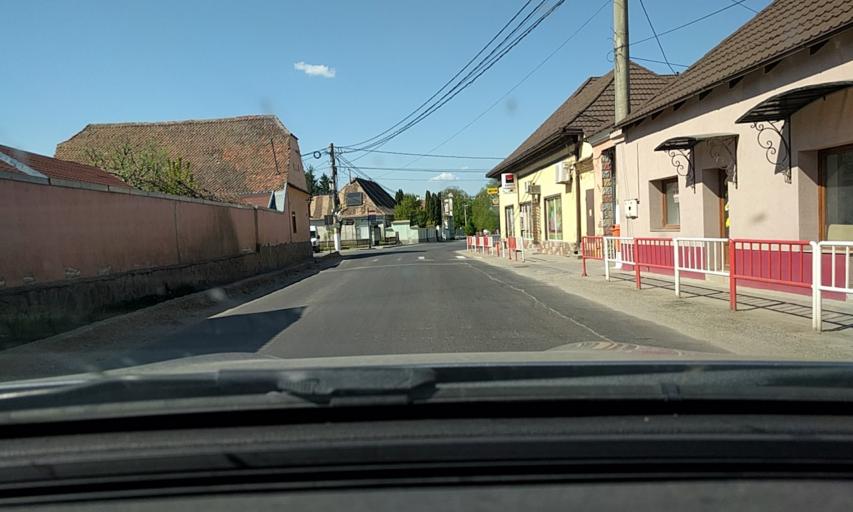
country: RO
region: Brasov
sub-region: Comuna Harman
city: Harman
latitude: 45.7132
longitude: 25.6845
